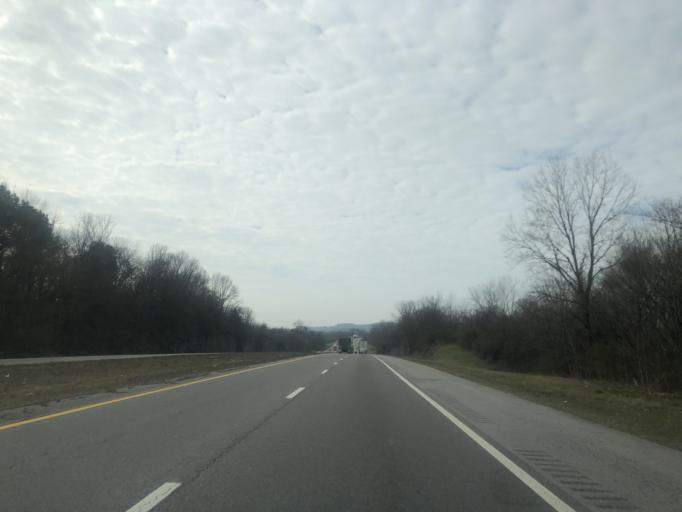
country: US
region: Tennessee
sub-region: Maury County
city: Columbia
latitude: 35.6350
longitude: -87.0507
